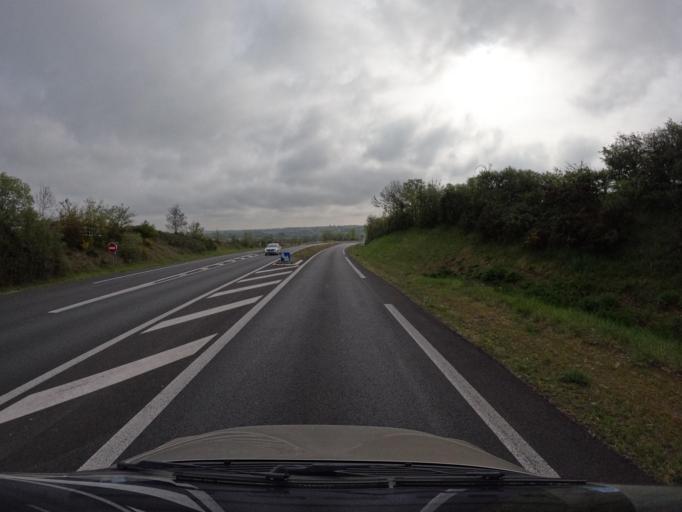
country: FR
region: Pays de la Loire
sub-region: Departement de Maine-et-Loire
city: Vihiers
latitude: 47.1402
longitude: -0.5635
